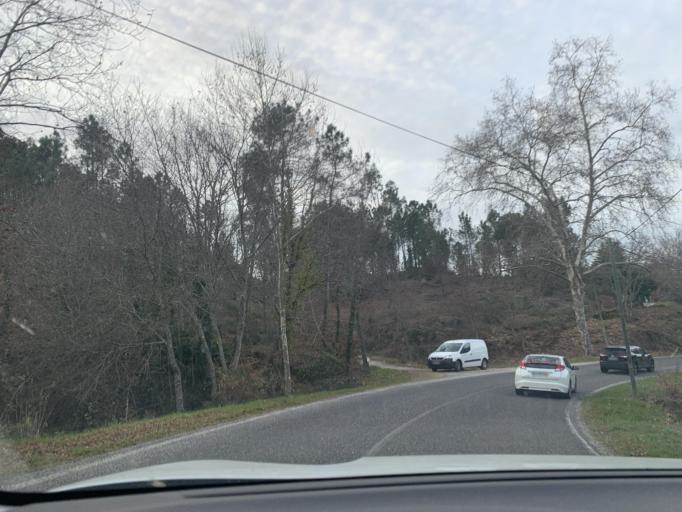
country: PT
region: Viseu
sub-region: Viseu
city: Viseu
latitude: 40.6000
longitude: -7.9937
